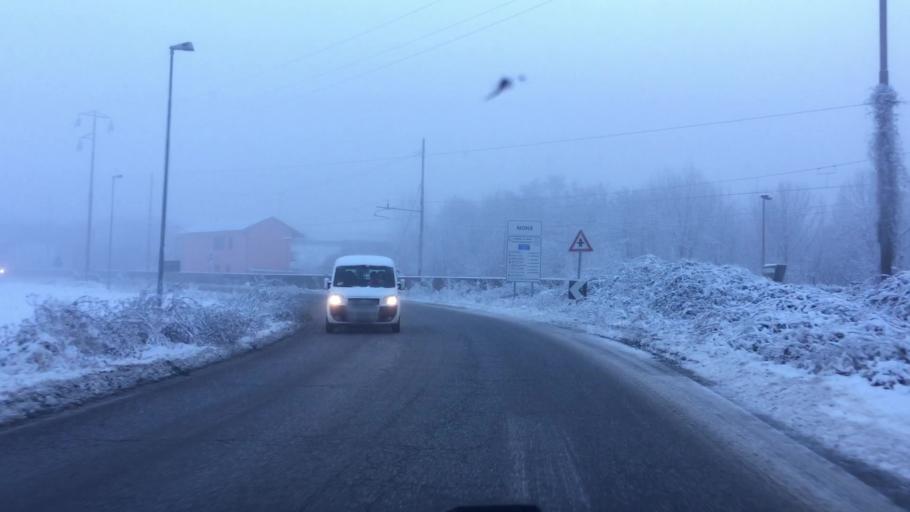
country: IT
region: Piedmont
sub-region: Provincia di Torino
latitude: 44.9378
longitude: 7.5341
